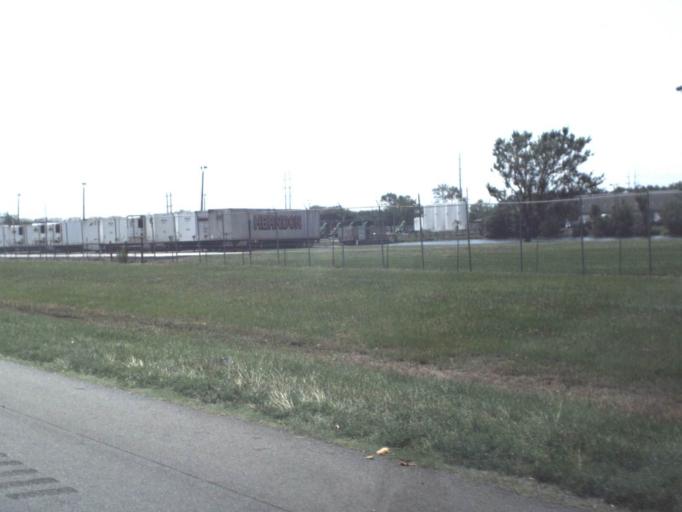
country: US
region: Florida
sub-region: Clay County
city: Bellair-Meadowbrook Terrace
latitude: 30.3129
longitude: -81.8153
